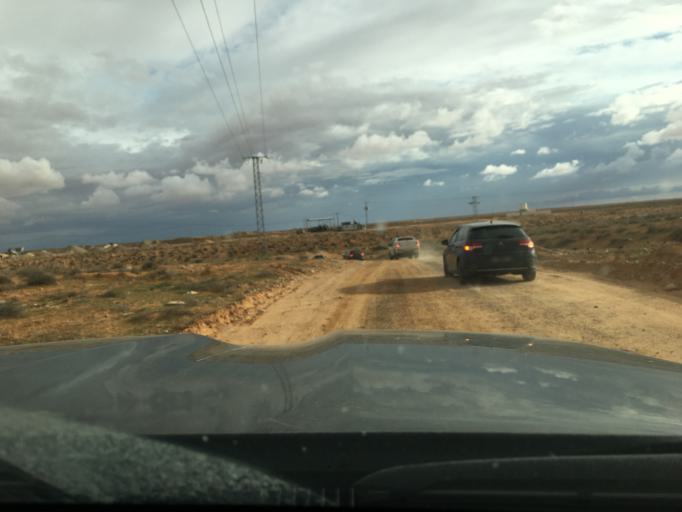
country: TN
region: Madanin
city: Medenine
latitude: 33.2692
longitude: 10.5688
